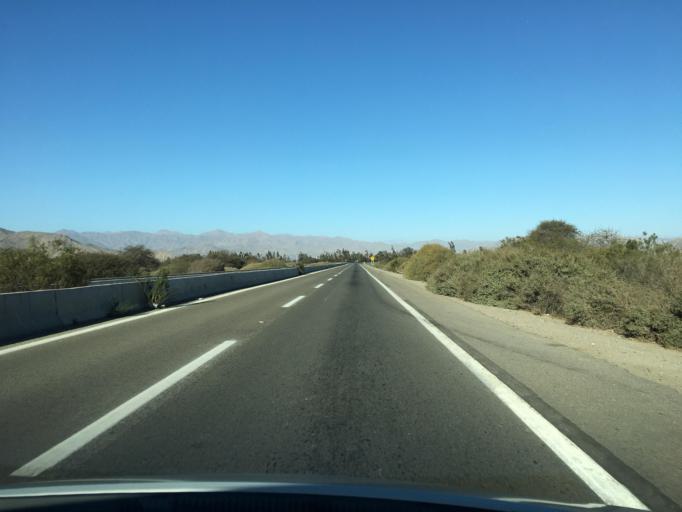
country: CL
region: Atacama
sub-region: Provincia de Copiapo
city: Copiapo
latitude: -27.2961
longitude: -70.4678
